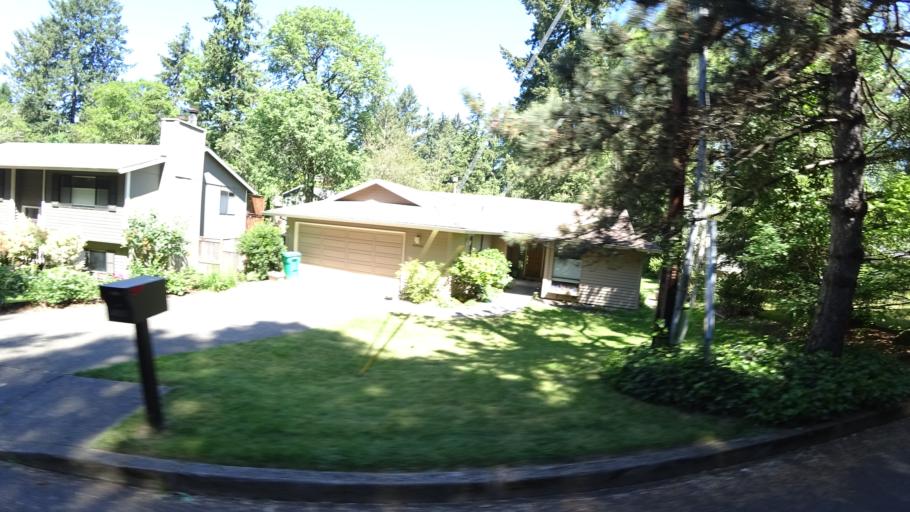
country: US
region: Oregon
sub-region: Washington County
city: Raleigh Hills
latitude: 45.4892
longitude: -122.7274
